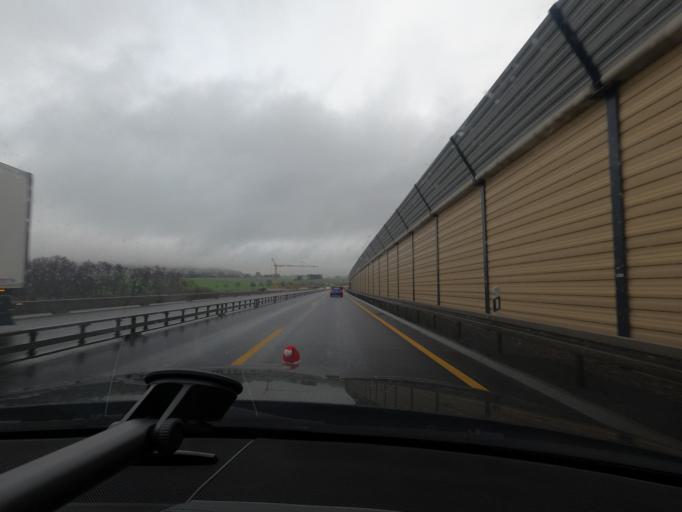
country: DE
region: Lower Saxony
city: Kalefeld
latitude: 51.7872
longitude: 10.0472
